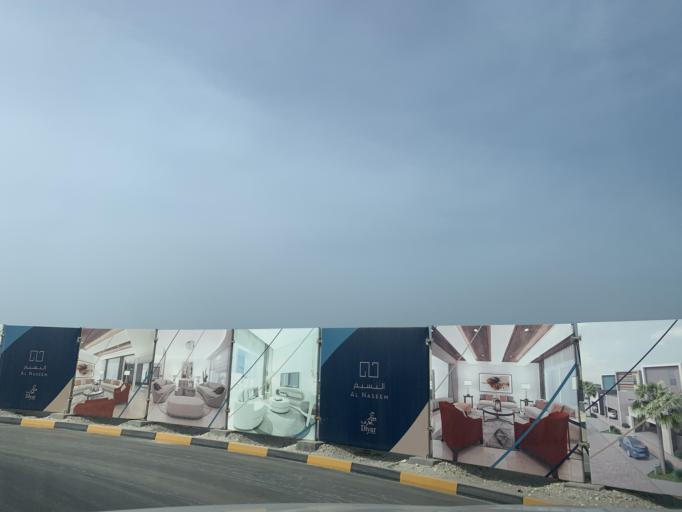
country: BH
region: Muharraq
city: Al Muharraq
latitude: 26.3145
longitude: 50.6371
